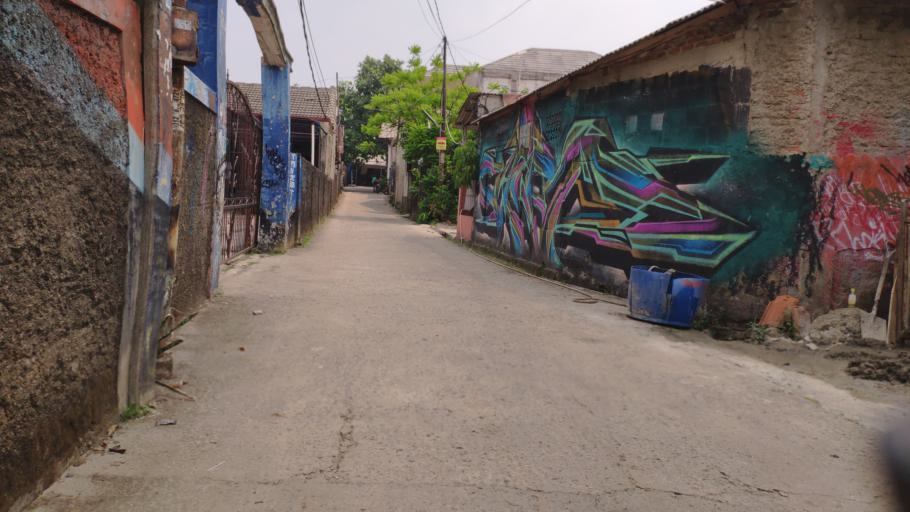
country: ID
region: West Java
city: Depok
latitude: -6.3675
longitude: 106.8061
